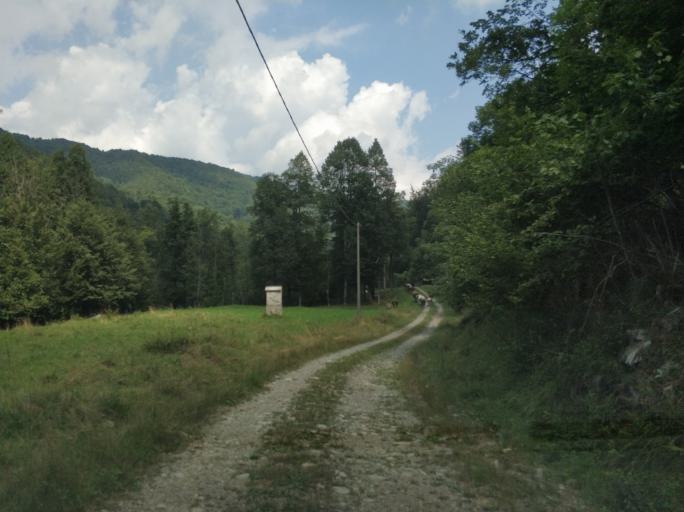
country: IT
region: Piedmont
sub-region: Provincia di Torino
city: Viu
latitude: 45.2103
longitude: 7.3939
